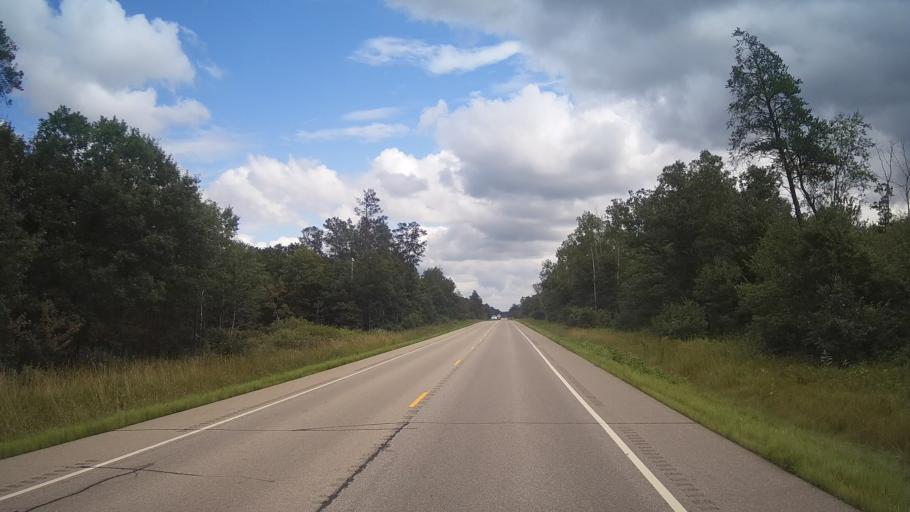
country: US
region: Wisconsin
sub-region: Adams County
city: Friendship
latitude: 44.0254
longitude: -89.7171
